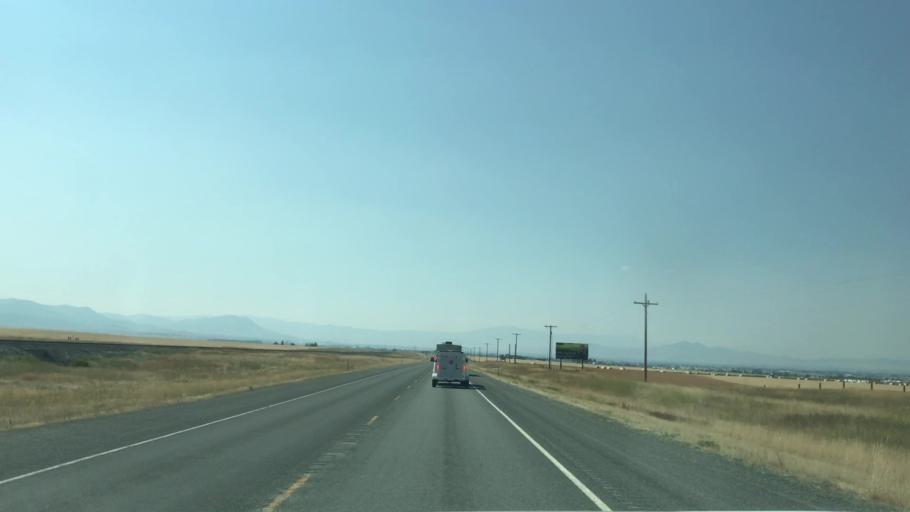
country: US
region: Montana
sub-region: Lewis and Clark County
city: East Helena
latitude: 46.5831
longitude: -111.8540
